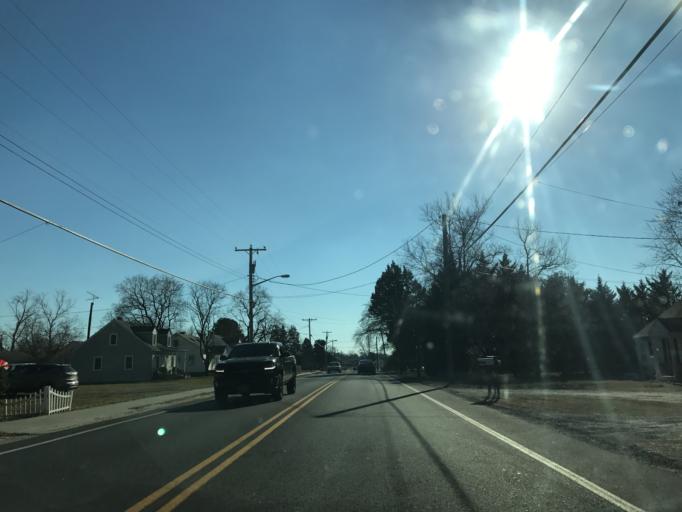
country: US
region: Maryland
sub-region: Caroline County
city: Denton
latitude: 38.8925
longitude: -75.8212
